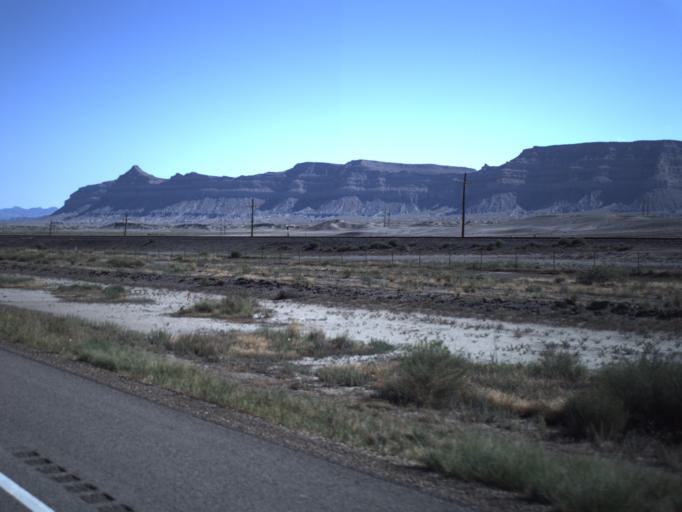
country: US
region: Utah
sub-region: Carbon County
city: East Carbon City
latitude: 39.0935
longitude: -110.3214
